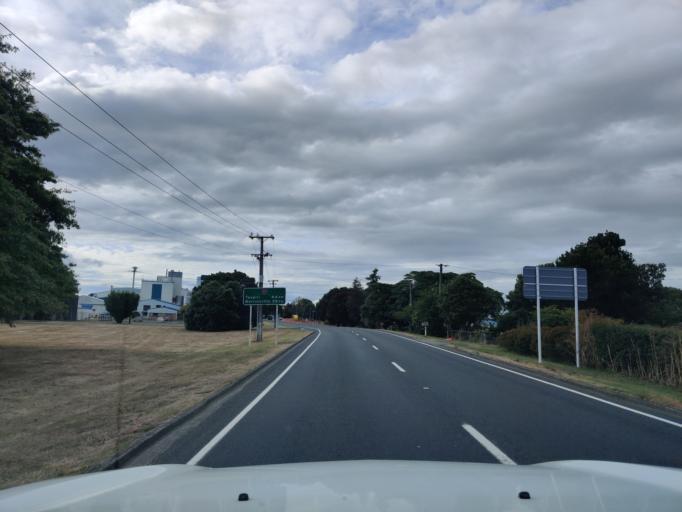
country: NZ
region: Waikato
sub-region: Waipa District
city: Cambridge
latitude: -37.8608
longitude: 175.4550
